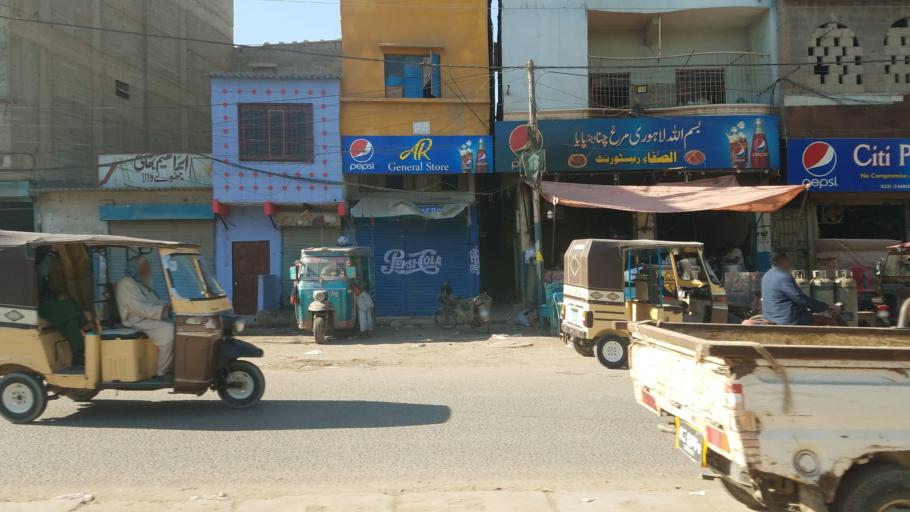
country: PK
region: Sindh
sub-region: Karachi District
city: Karachi
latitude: 24.9221
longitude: 67.0497
